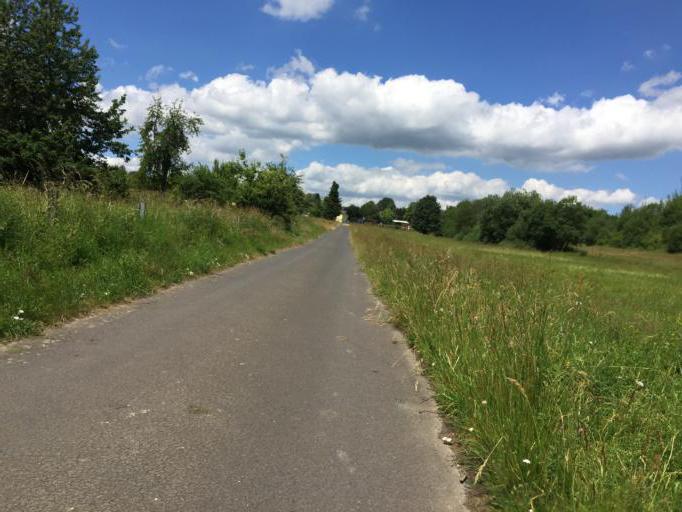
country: DE
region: Rheinland-Pfalz
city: Girod
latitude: 50.4448
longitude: 7.9105
